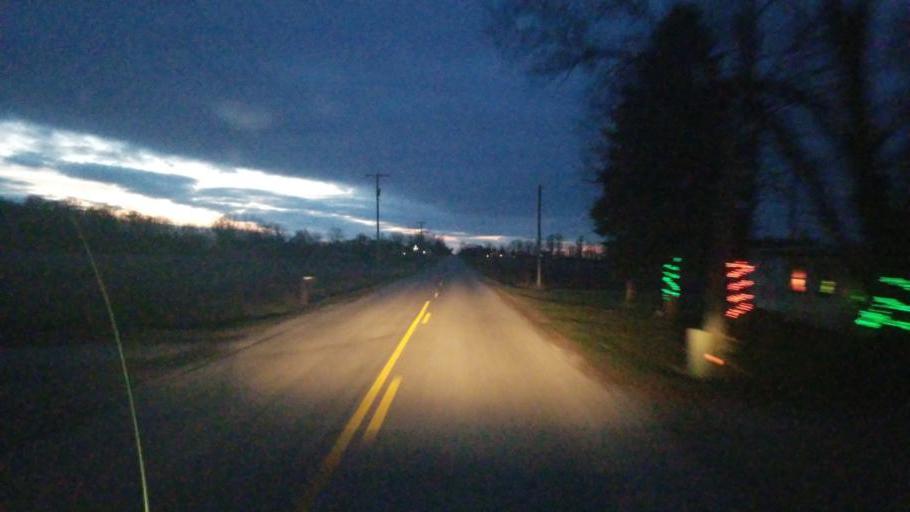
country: US
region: Ohio
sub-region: Marion County
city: Prospect
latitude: 40.4674
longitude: -83.1958
